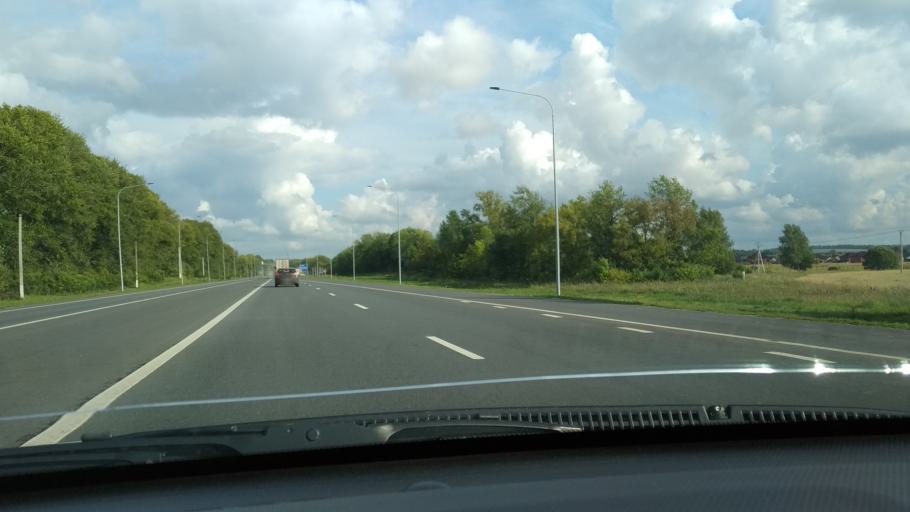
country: RU
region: Tatarstan
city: Stolbishchi
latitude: 55.6591
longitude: 49.3036
